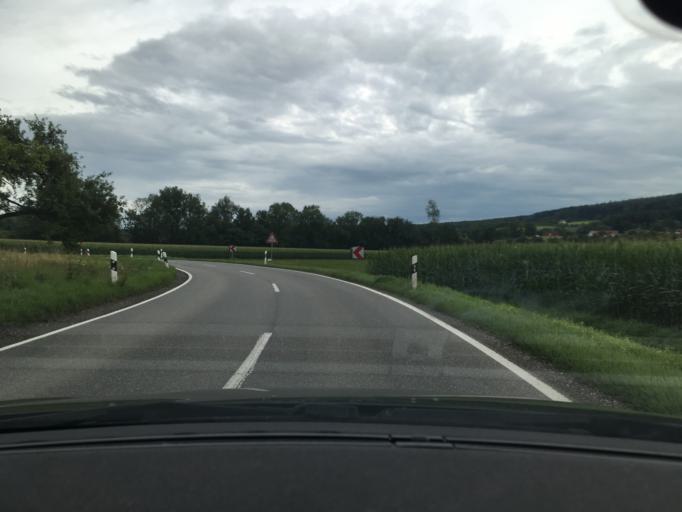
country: DE
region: Baden-Wuerttemberg
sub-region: Tuebingen Region
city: Markdorf
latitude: 47.7690
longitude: 9.4232
